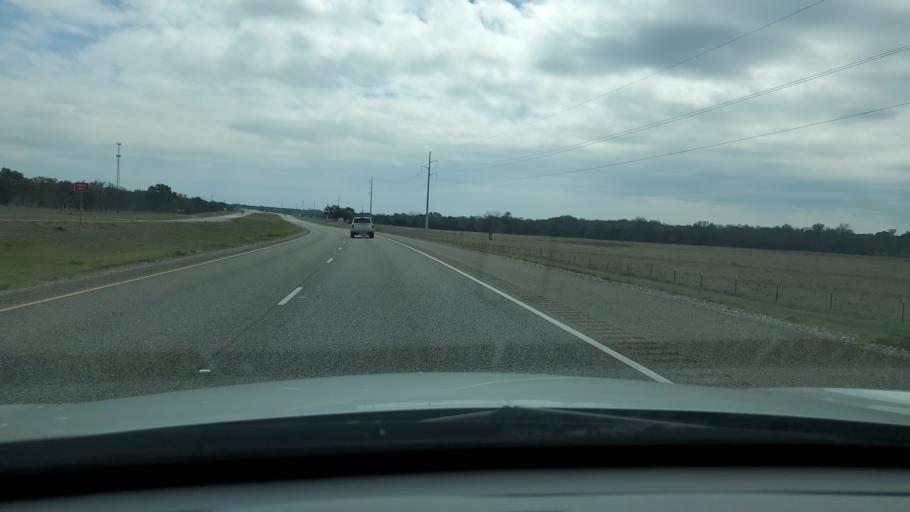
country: US
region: Texas
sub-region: Williamson County
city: Florence
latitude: 30.7701
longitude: -97.7565
